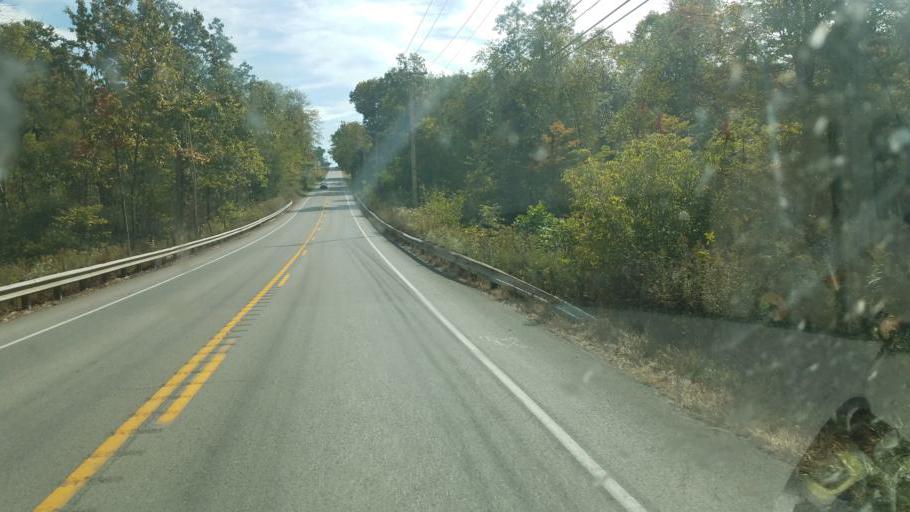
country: US
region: Pennsylvania
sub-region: Mercer County
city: Mercer
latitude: 41.3338
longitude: -80.2285
